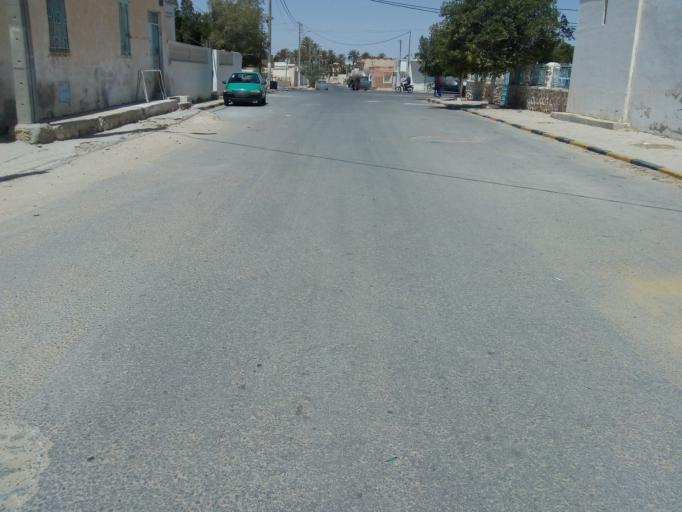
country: TN
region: Qabis
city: Gabes
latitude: 33.9573
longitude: 10.0134
